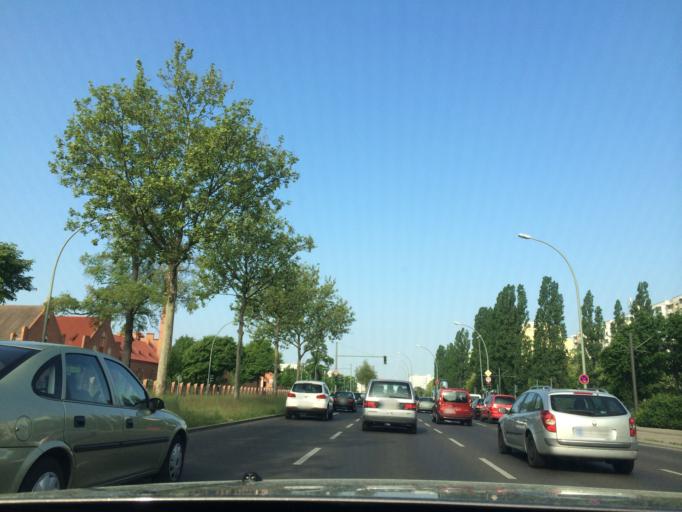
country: DE
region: Berlin
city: Alt-Hohenschoenhausen
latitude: 52.5341
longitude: 13.4931
